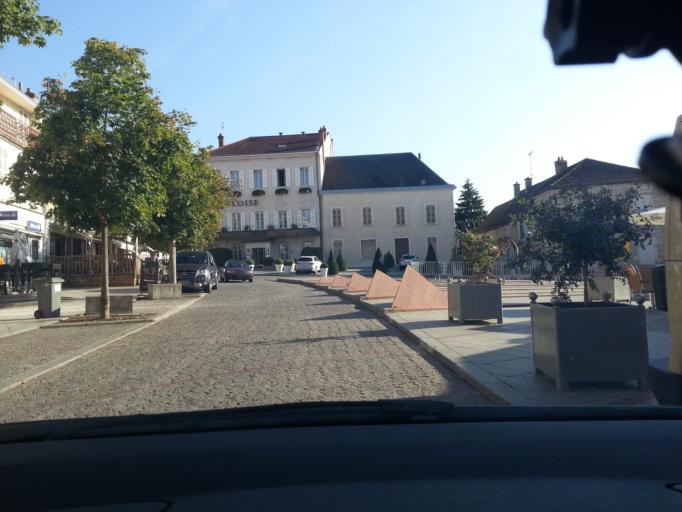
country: FR
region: Bourgogne
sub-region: Departement de Saone-et-Loire
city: Chagny
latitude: 46.9084
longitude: 4.7532
